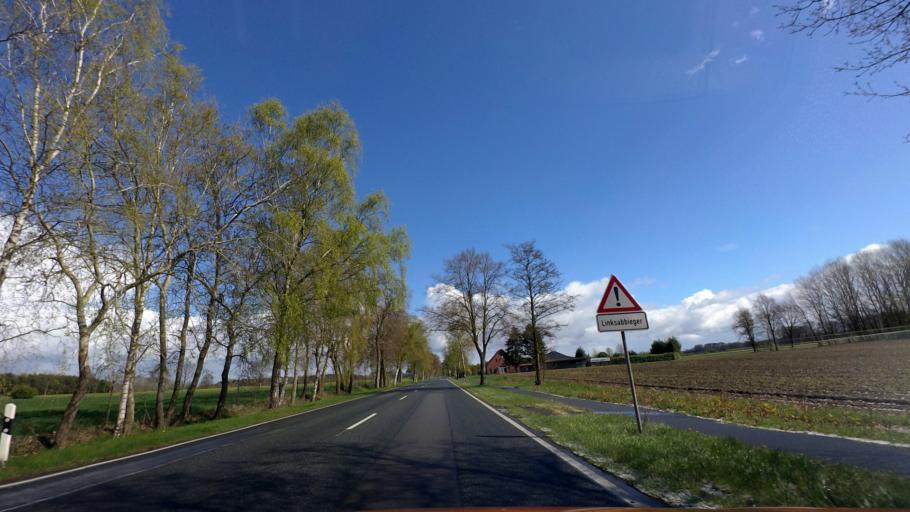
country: DE
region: Lower Saxony
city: Ottersberg
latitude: 53.0737
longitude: 9.0994
